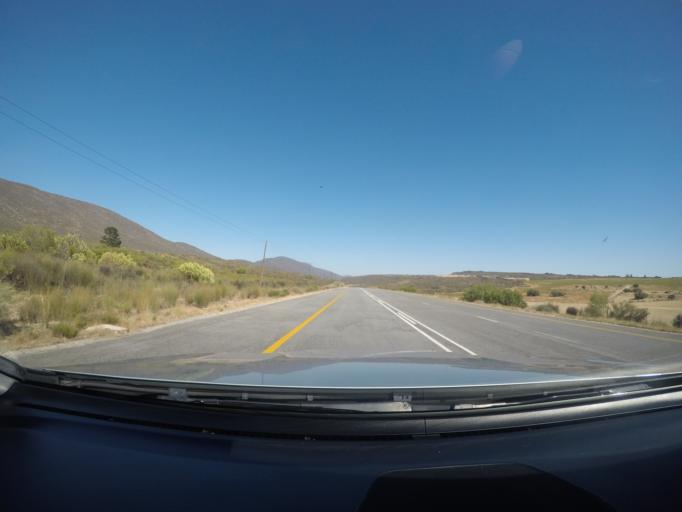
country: ZA
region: Western Cape
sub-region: West Coast District Municipality
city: Clanwilliam
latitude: -32.2711
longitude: 18.8801
